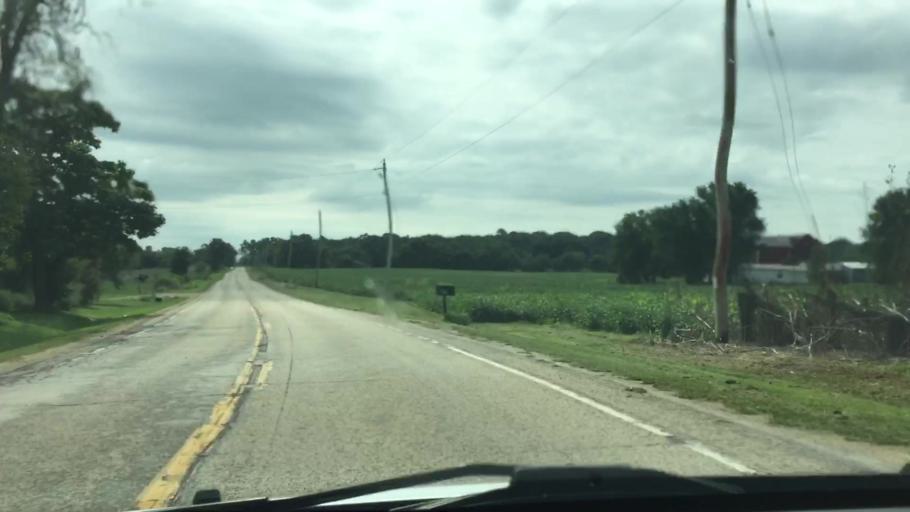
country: US
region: Wisconsin
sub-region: Dane County
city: Belleville
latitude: 42.8922
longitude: -89.4827
